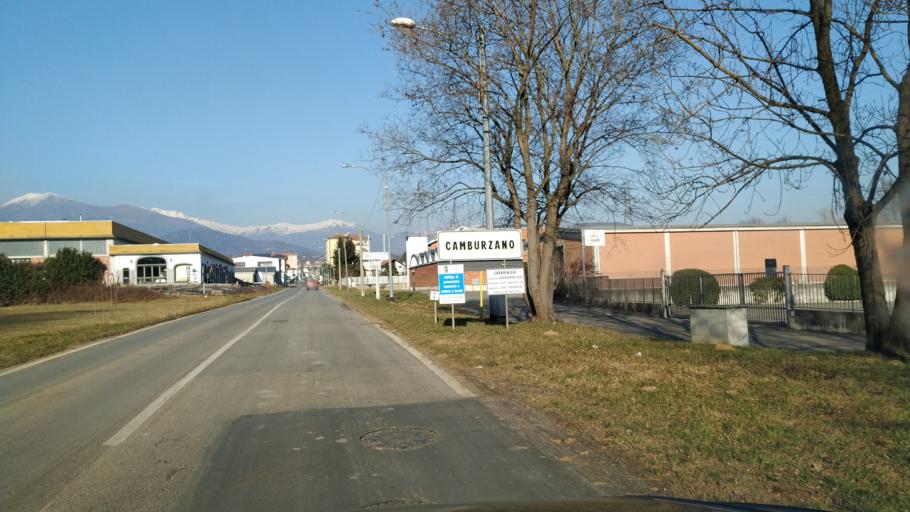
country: IT
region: Piedmont
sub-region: Provincia di Biella
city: Mongrando
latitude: 45.5382
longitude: 8.0122
